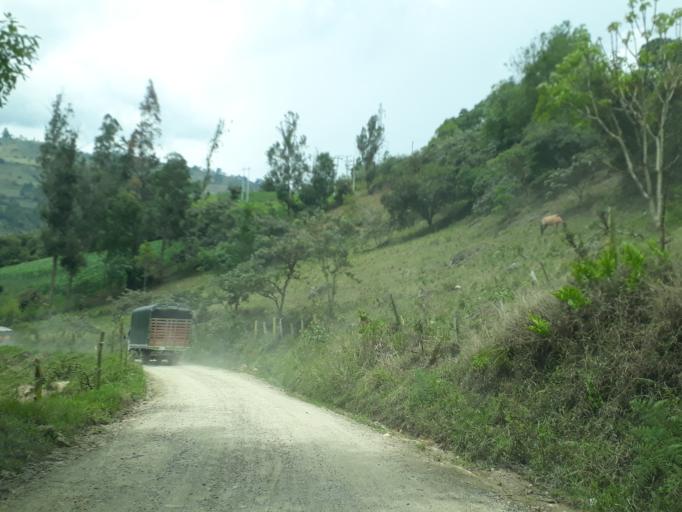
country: CO
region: Cundinamarca
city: Macheta
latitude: 5.0788
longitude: -73.5815
